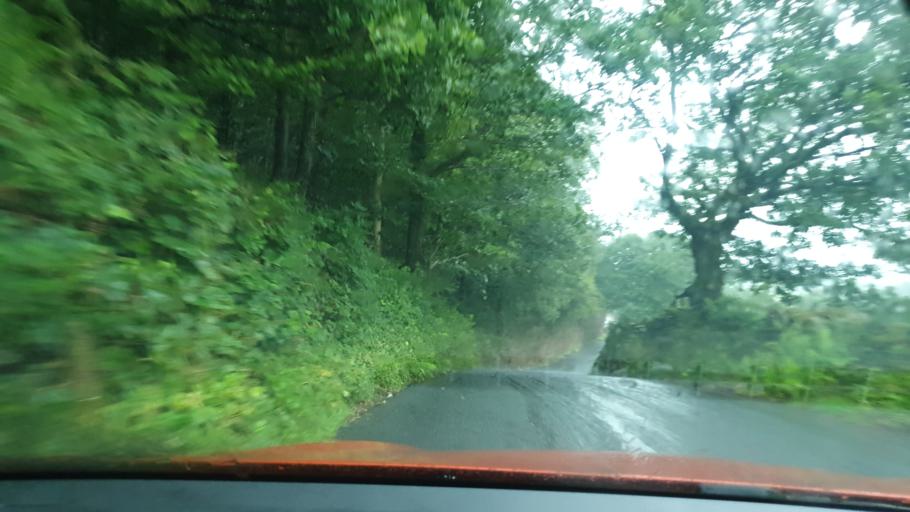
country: GB
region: England
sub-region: Cumbria
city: Millom
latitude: 54.2881
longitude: -3.2327
